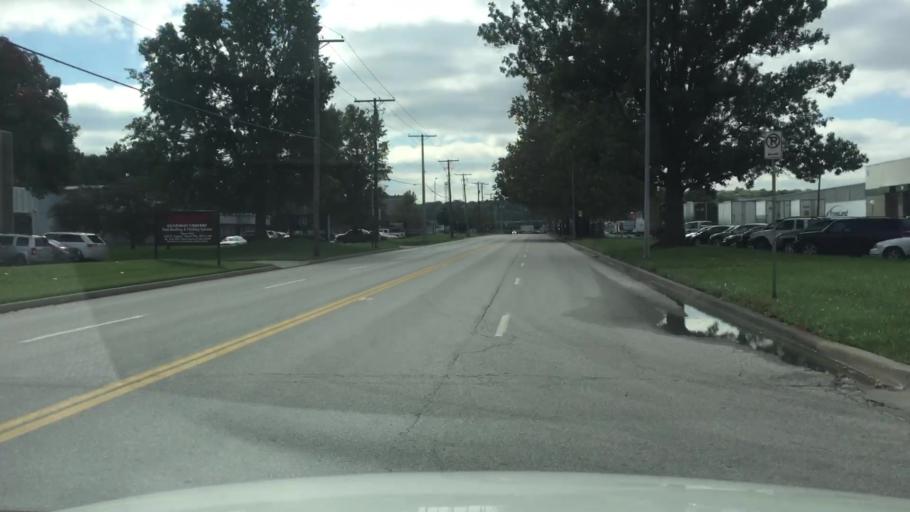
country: US
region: Missouri
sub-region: Clay County
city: North Kansas City
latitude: 39.1346
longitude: -94.5141
